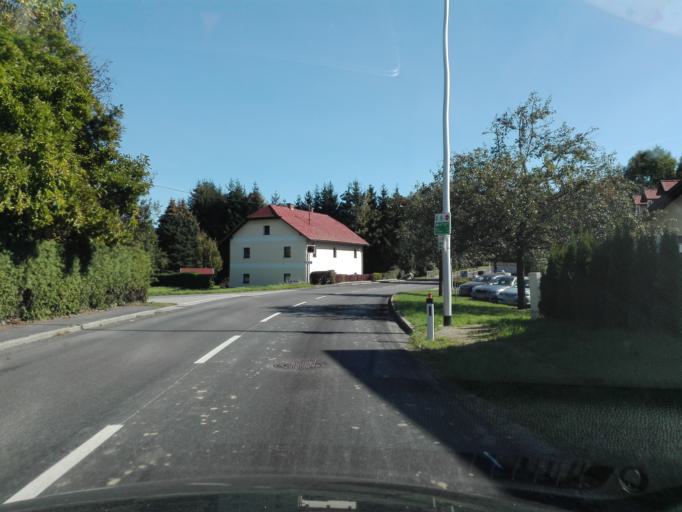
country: AT
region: Upper Austria
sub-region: Politischer Bezirk Linz-Land
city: Sankt Florian
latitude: 48.2164
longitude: 14.3517
